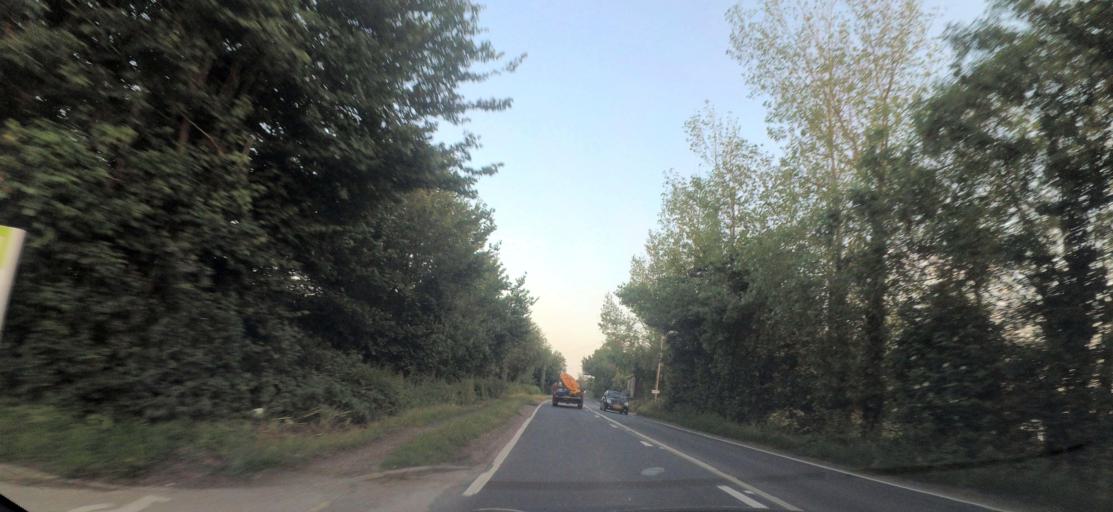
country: GB
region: England
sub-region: West Sussex
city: Selsey
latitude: 50.7534
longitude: -0.7820
